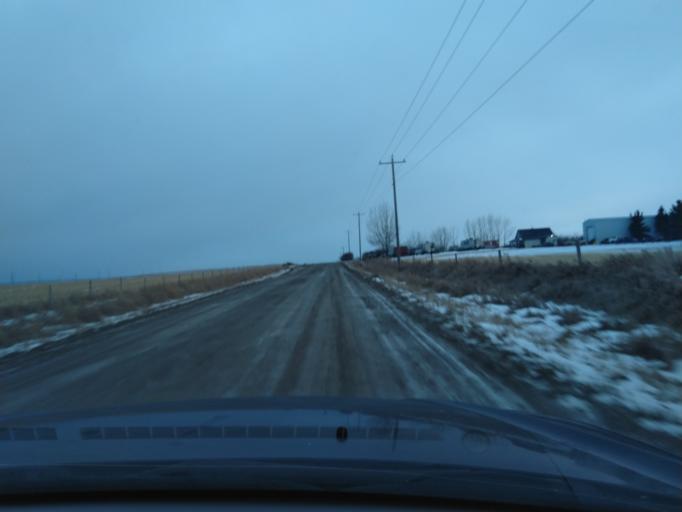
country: CA
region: Alberta
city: Airdrie
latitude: 51.1834
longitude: -114.0264
